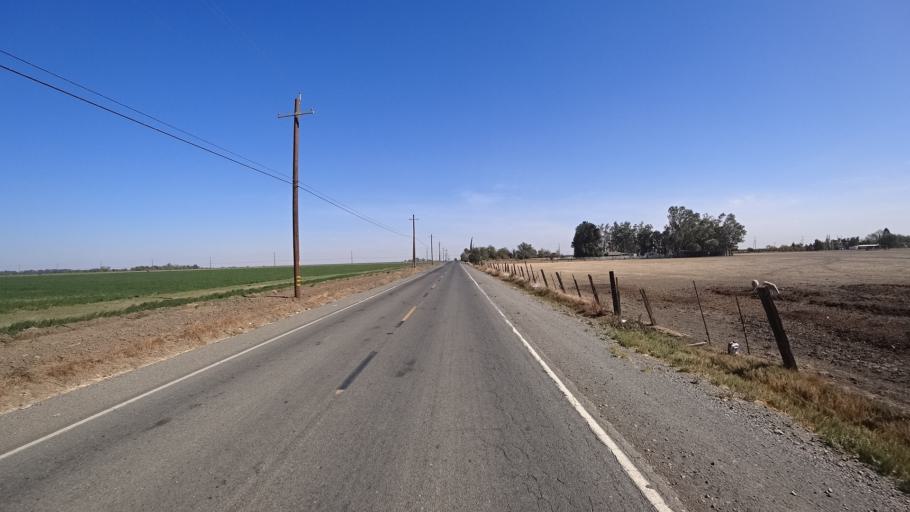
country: US
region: California
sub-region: Yolo County
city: Woodland
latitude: 38.6188
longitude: -121.7339
